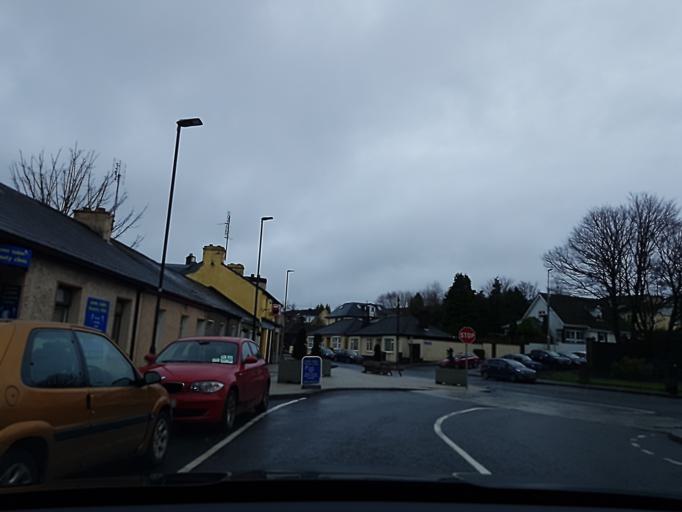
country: IE
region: Connaught
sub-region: Maigh Eo
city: Castlebar
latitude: 53.8599
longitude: -9.2984
